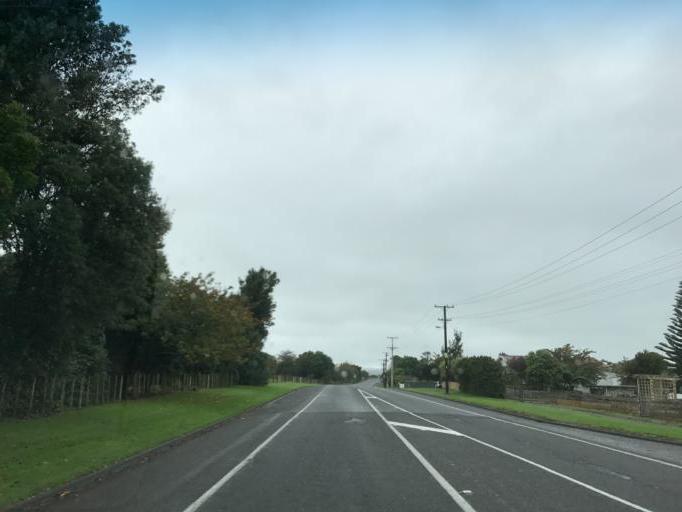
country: NZ
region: Taranaki
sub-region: South Taranaki District
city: Patea
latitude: -39.7638
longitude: 174.6357
